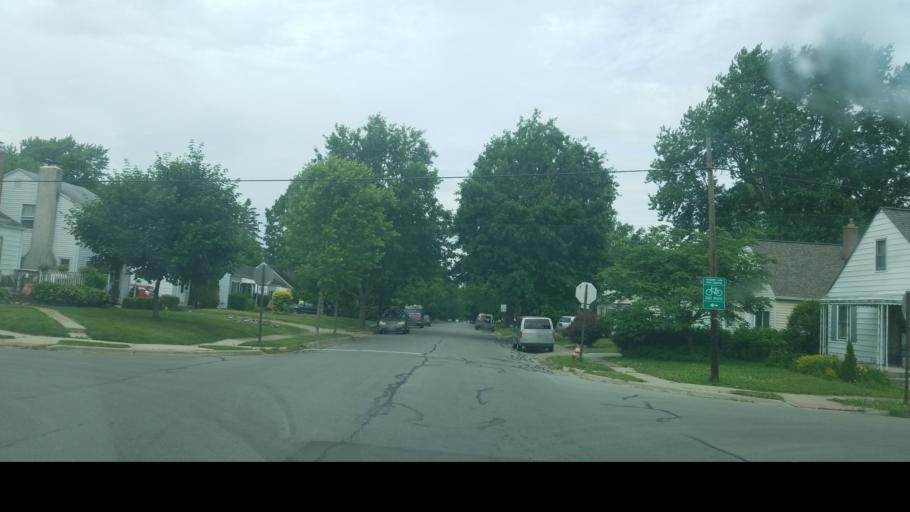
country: US
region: Ohio
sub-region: Franklin County
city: Worthington
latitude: 40.0753
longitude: -83.0119
